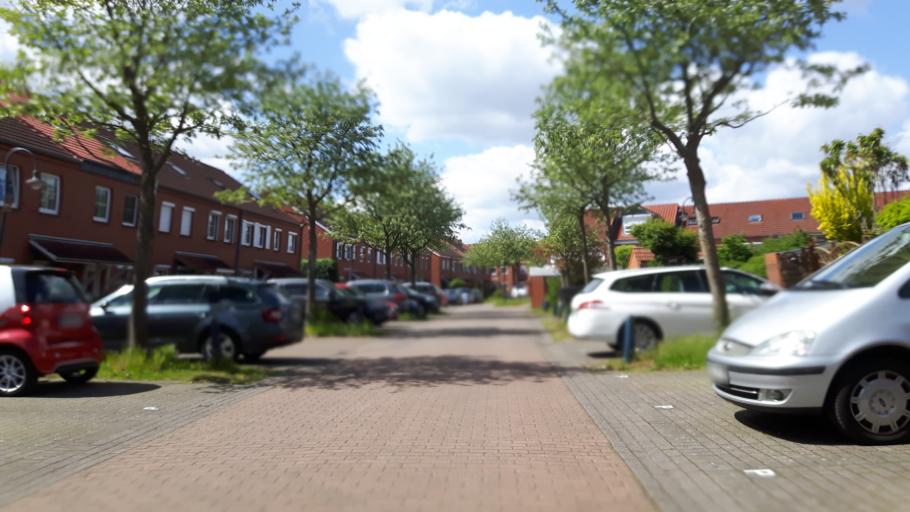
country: DE
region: Bremen
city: Bremen
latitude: 53.0441
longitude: 8.8483
